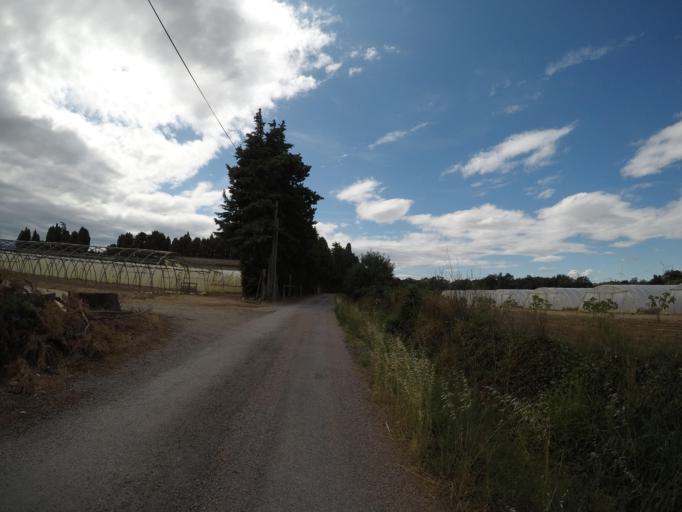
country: FR
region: Languedoc-Roussillon
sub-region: Departement des Pyrenees-Orientales
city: Pezilla-la-Riviere
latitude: 42.6995
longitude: 2.7867
